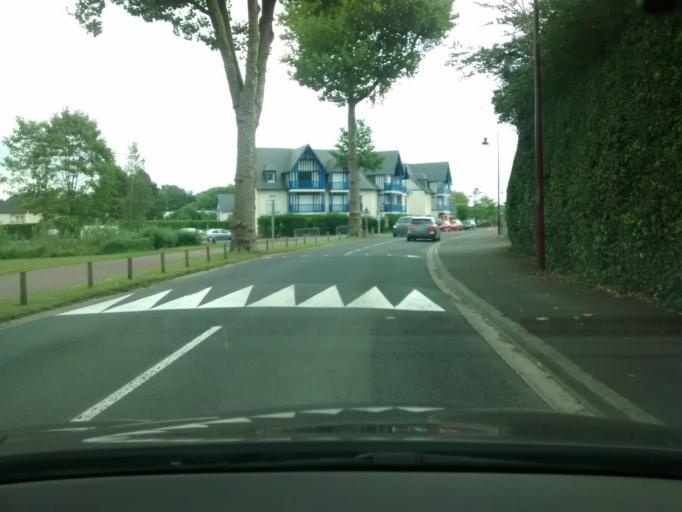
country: FR
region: Lower Normandy
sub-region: Departement du Calvados
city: Touques
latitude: 49.3399
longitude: 0.0912
